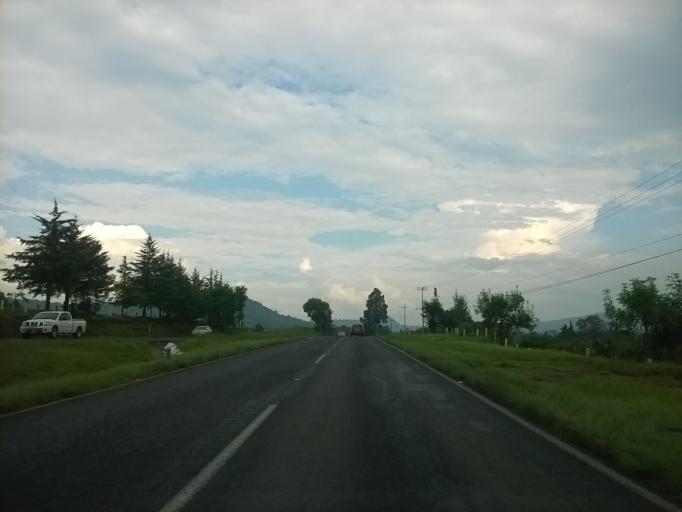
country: MX
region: Michoacan
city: Cuanajo
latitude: 19.5343
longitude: -101.5046
